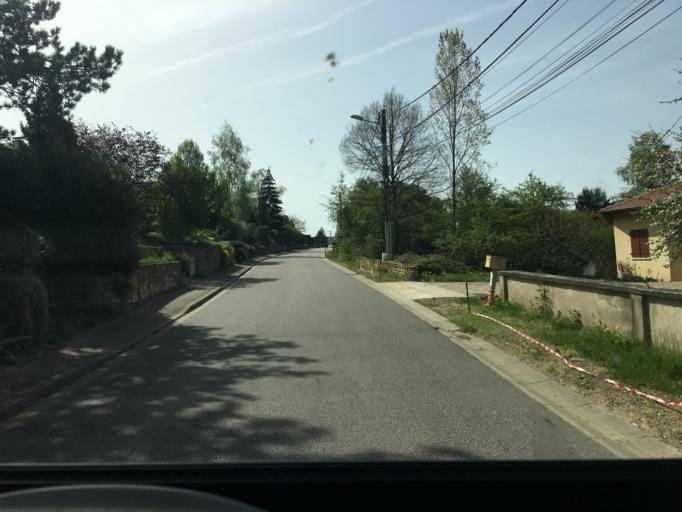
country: FR
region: Lorraine
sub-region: Departement de Meurthe-et-Moselle
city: Chaligny
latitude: 48.6411
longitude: 6.0439
